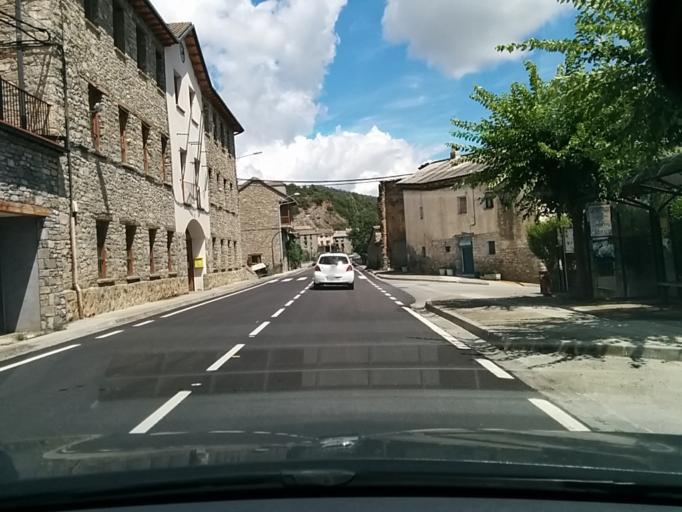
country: ES
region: Aragon
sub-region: Provincia de Huesca
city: Labuerda
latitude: 42.4500
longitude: 0.1338
